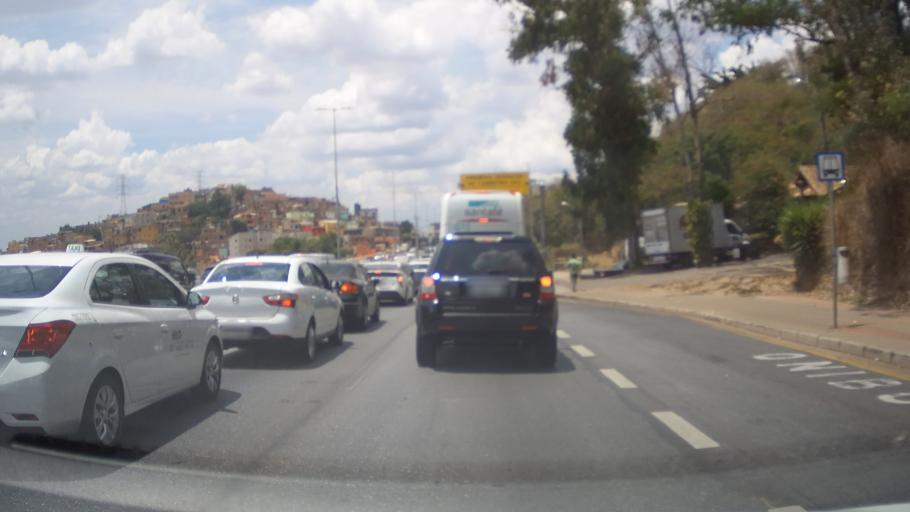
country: BR
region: Minas Gerais
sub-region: Belo Horizonte
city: Belo Horizonte
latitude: -19.9598
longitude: -43.9438
